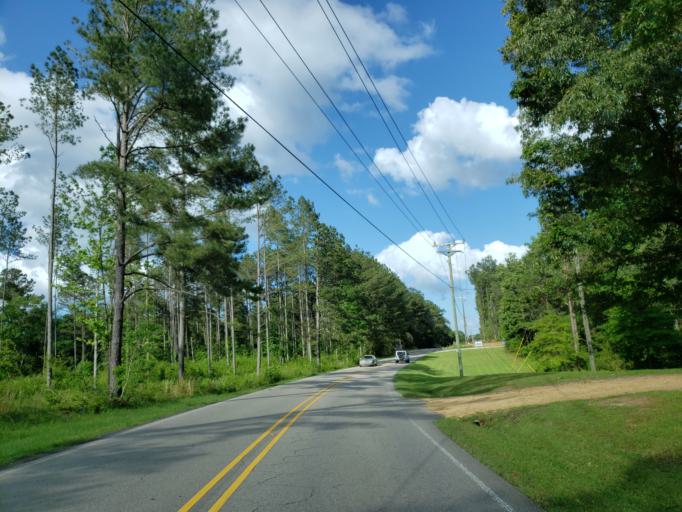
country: US
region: Mississippi
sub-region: Lamar County
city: West Hattiesburg
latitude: 31.2860
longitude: -89.4656
